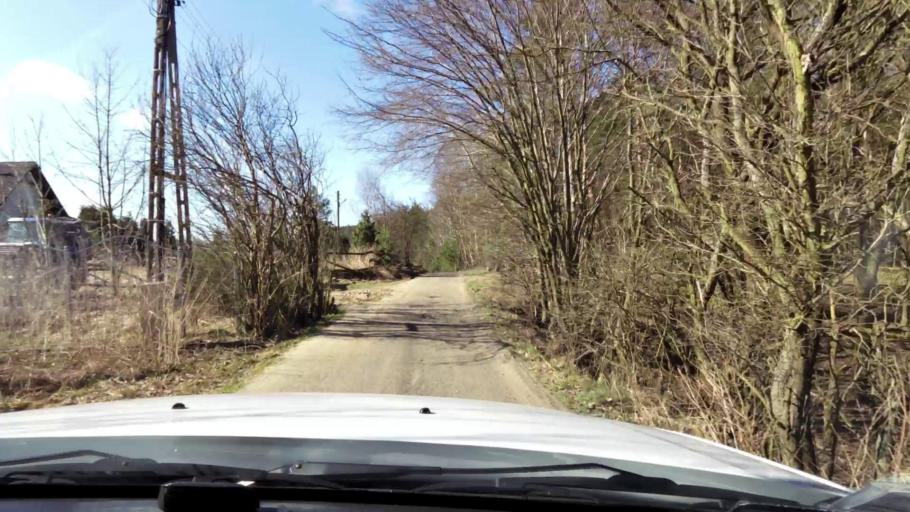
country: PL
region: West Pomeranian Voivodeship
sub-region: Powiat gryfinski
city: Gryfino
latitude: 53.2206
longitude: 14.5185
